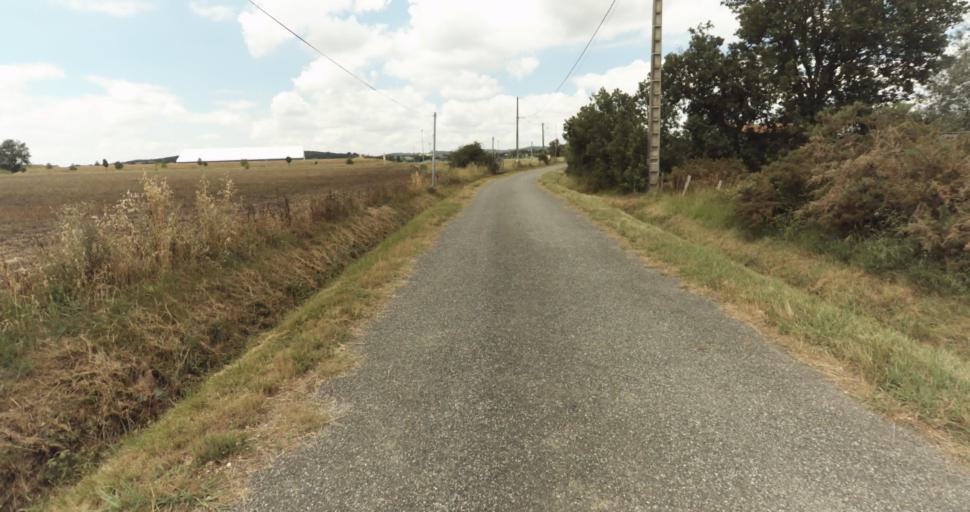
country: FR
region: Midi-Pyrenees
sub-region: Departement de la Haute-Garonne
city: Fontenilles
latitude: 43.5542
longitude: 1.1819
